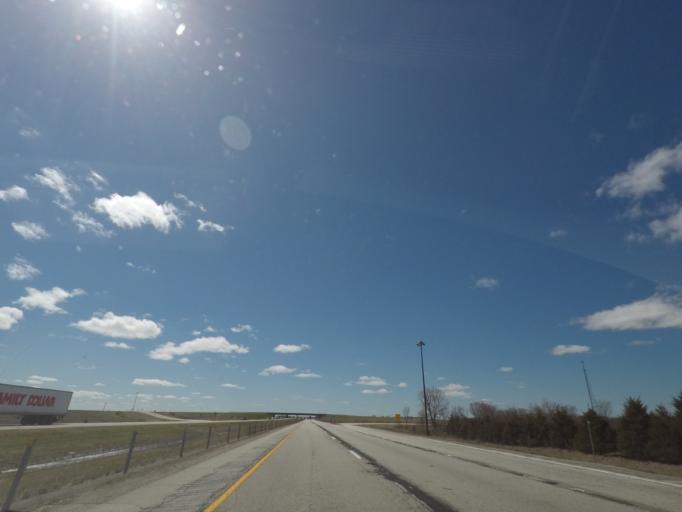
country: US
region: Illinois
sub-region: Livingston County
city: Odell
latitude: 41.0104
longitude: -88.5353
